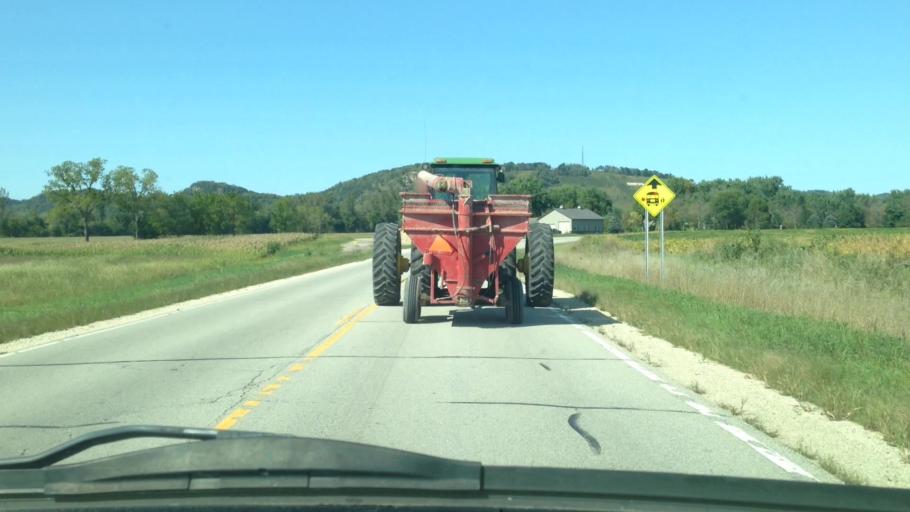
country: US
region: Minnesota
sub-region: Fillmore County
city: Rushford
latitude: 43.7912
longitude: -91.7652
